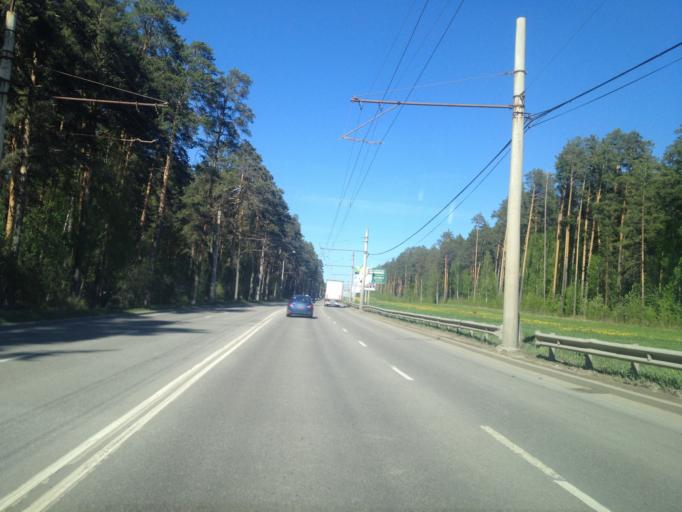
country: RU
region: Sverdlovsk
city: Sovkhoznyy
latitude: 56.7816
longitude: 60.5606
